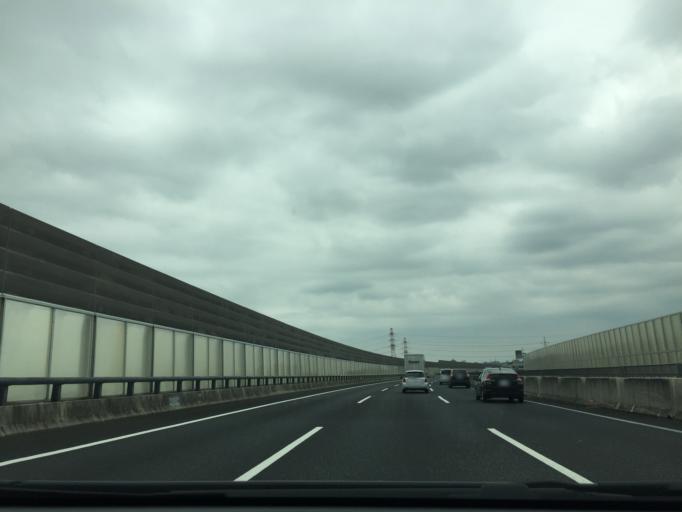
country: JP
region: Aichi
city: Chiryu
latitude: 35.0423
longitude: 137.0321
